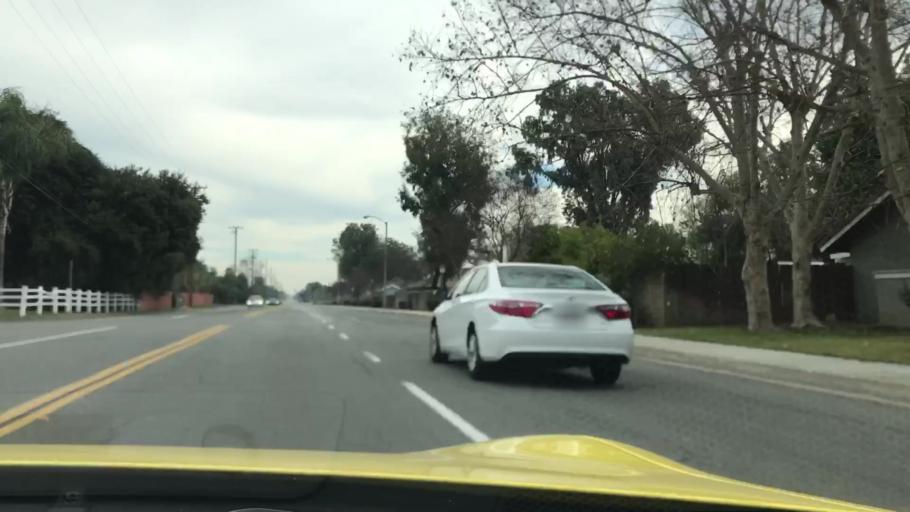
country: US
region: California
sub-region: San Bernardino County
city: Chino Hills
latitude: 34.0115
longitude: -117.7288
